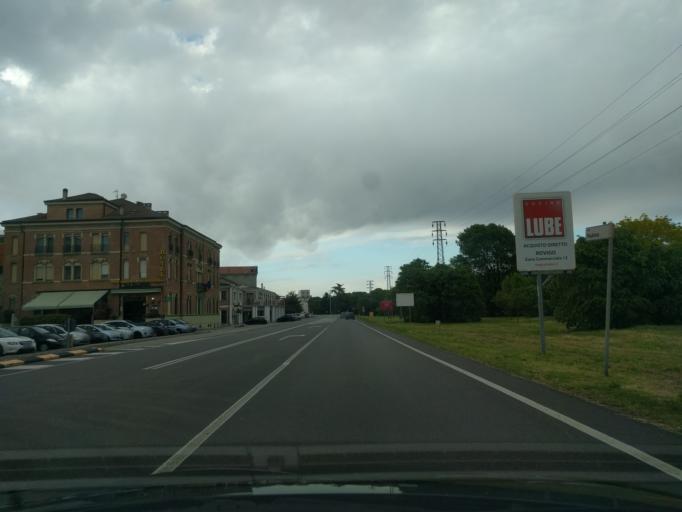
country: IT
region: Veneto
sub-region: Provincia di Rovigo
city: Santa Maria Maddalena
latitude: 44.8803
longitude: 11.6078
